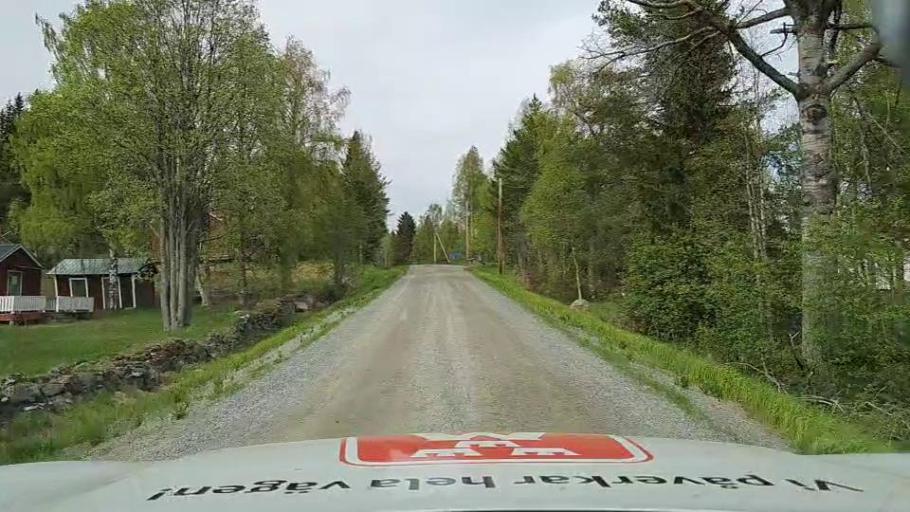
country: SE
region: Jaemtland
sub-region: OEstersunds Kommun
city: Brunflo
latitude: 62.6131
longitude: 14.9455
